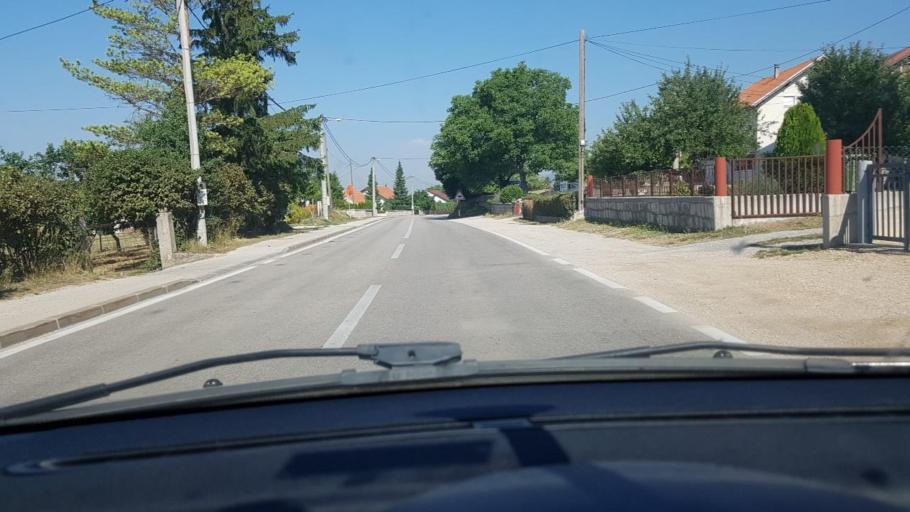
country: BA
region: Federation of Bosnia and Herzegovina
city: Livno
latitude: 43.8330
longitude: 16.9872
